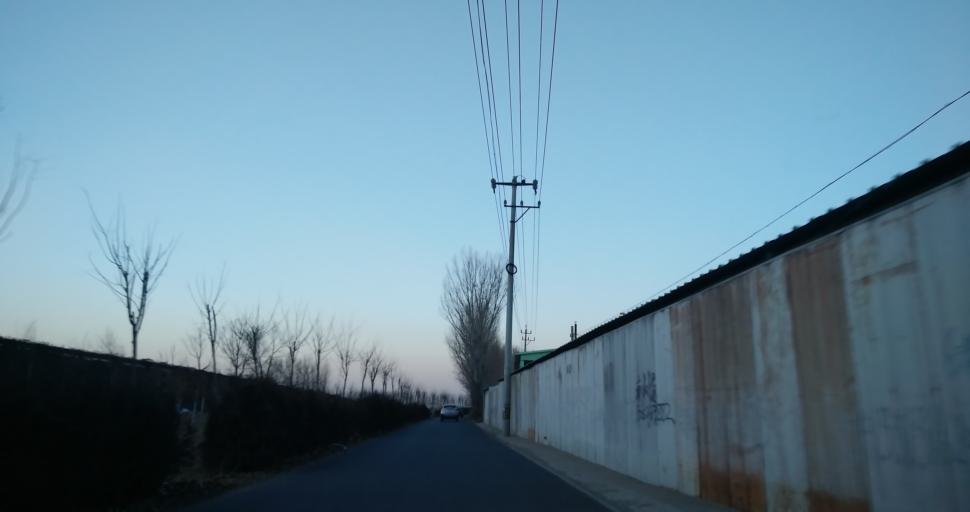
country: CN
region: Beijing
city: Yinghai
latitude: 39.7285
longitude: 116.4697
